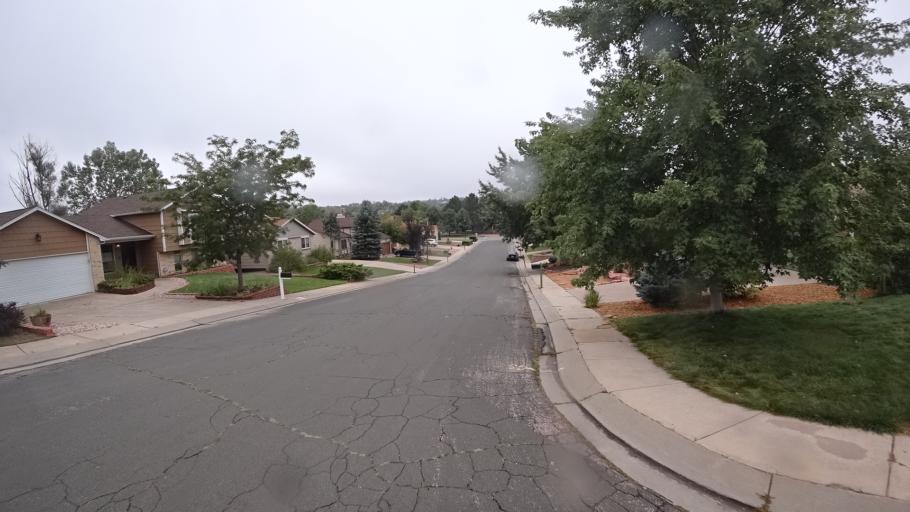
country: US
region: Colorado
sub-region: El Paso County
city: Cimarron Hills
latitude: 38.9326
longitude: -104.7676
